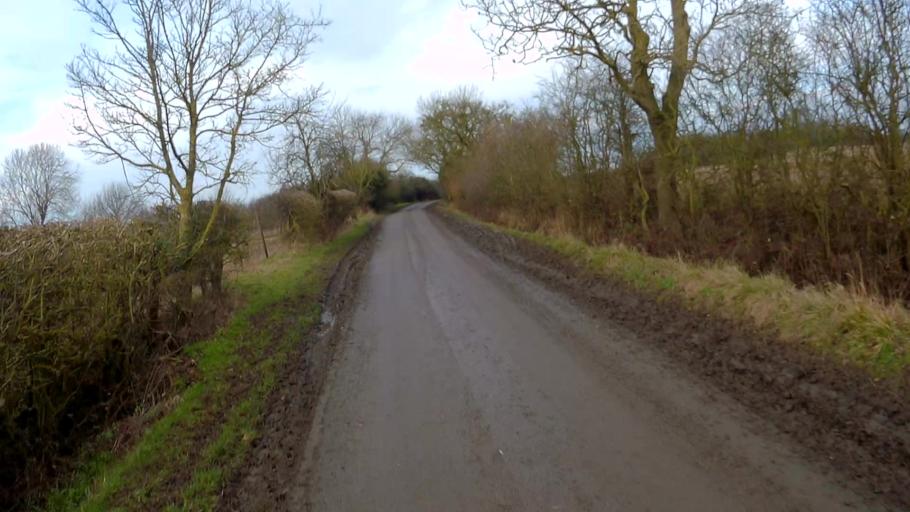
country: GB
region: England
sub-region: Lincolnshire
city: Bourne
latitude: 52.8132
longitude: -0.4362
